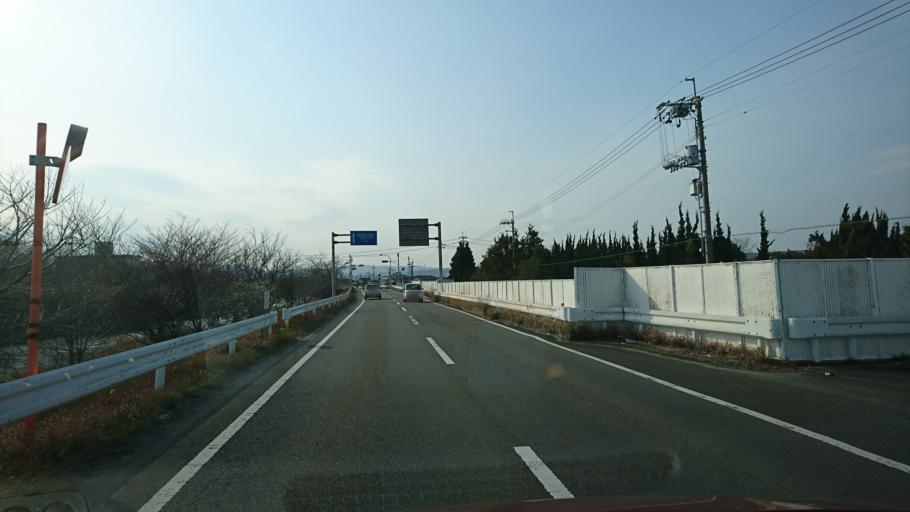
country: JP
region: Ehime
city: Saijo
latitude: 34.0380
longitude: 133.0294
